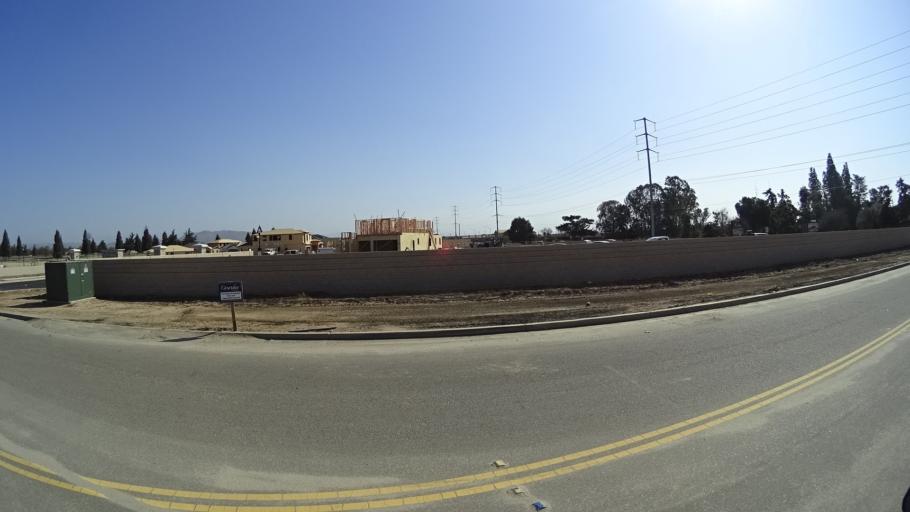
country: US
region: California
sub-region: Fresno County
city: Clovis
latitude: 36.8964
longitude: -119.7388
